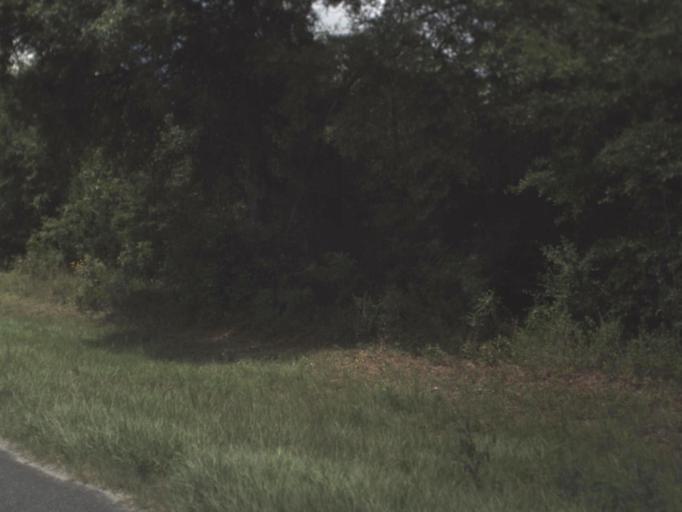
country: US
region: Florida
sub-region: Alachua County
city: High Springs
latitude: 29.8829
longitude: -82.8598
